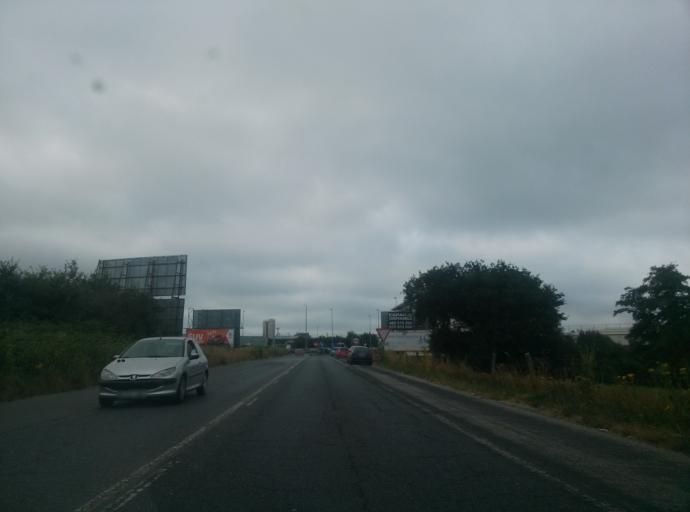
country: ES
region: Galicia
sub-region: Provincia de Lugo
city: Lugo
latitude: 43.0419
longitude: -7.5688
